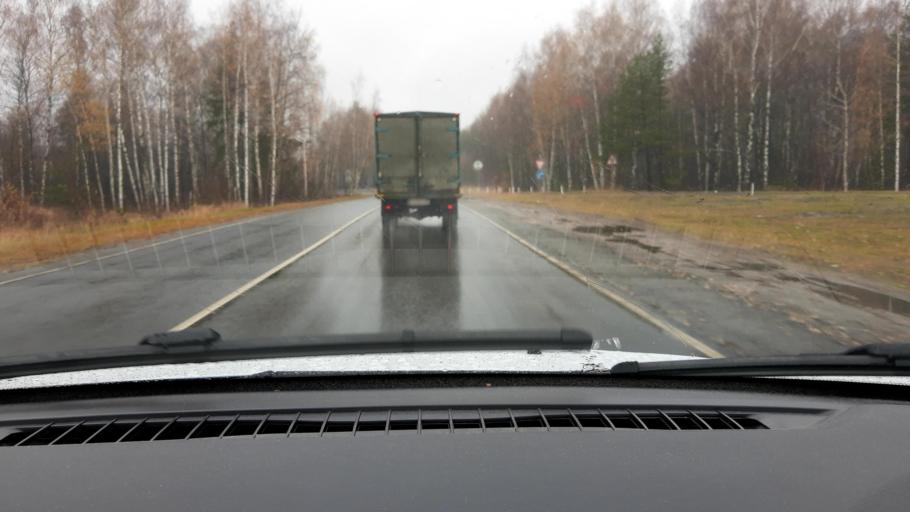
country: RU
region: Nizjnij Novgorod
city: Gorbatovka
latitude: 56.2624
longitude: 43.7025
